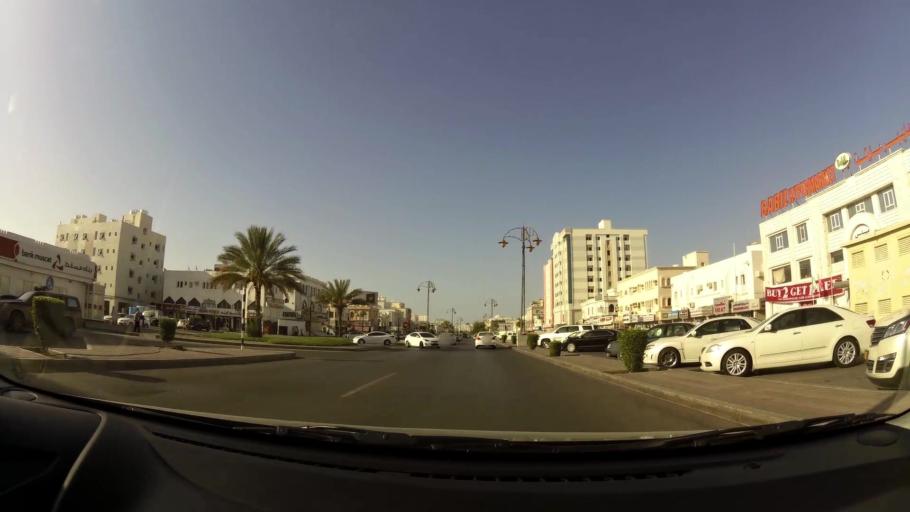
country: OM
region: Muhafazat Masqat
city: As Sib al Jadidah
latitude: 23.6315
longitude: 58.1984
